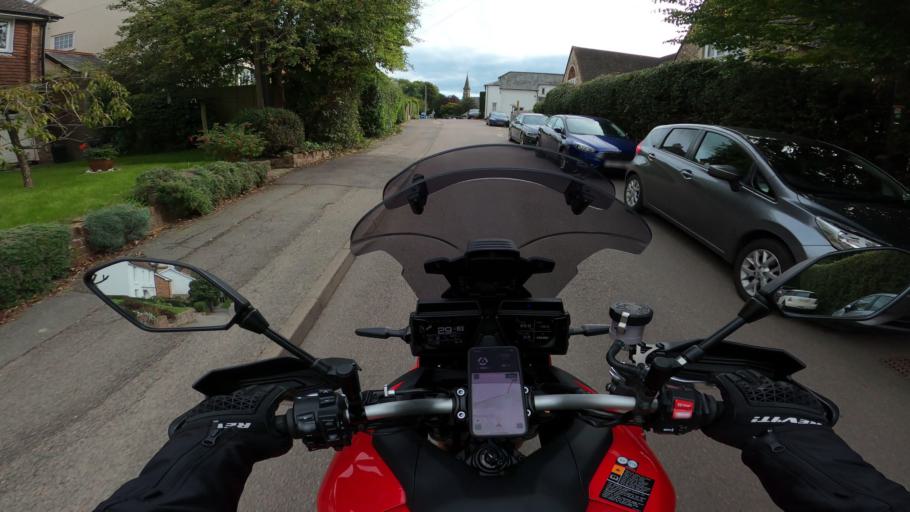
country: GB
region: England
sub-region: Kent
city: Westerham
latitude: 51.2474
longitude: 0.1274
